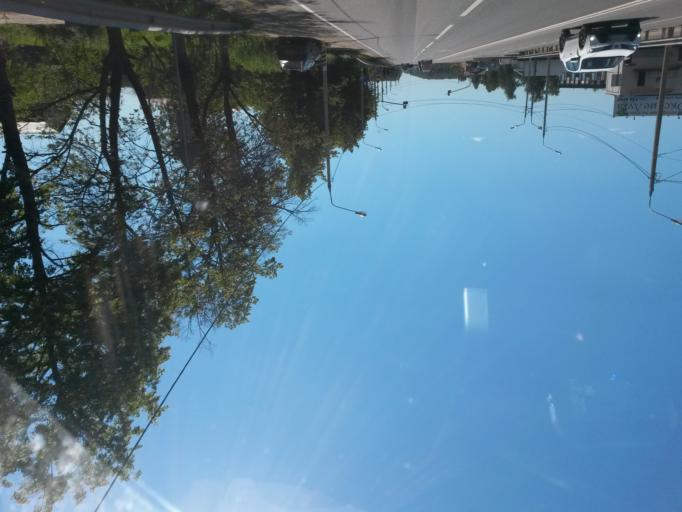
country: RU
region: Moskovskaya
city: Proletarskiy
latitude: 55.0282
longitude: 37.4274
